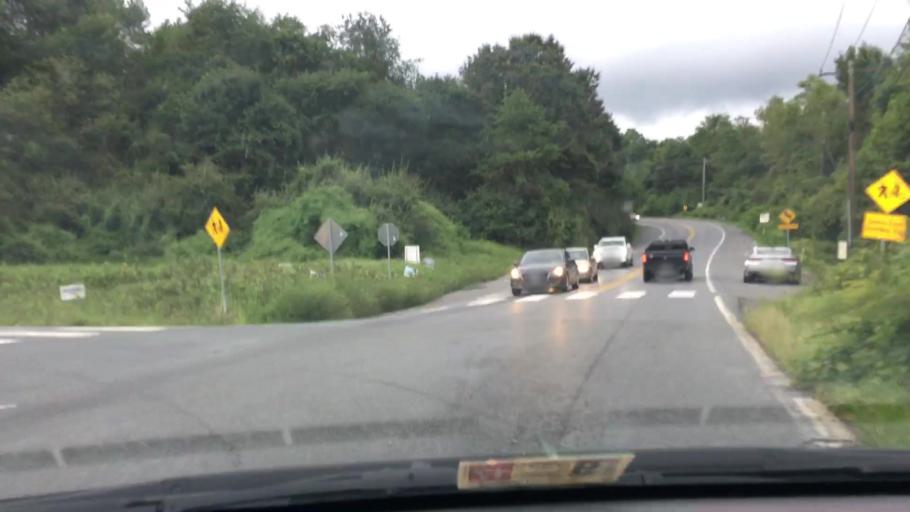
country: US
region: Maryland
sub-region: Montgomery County
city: Montgomery Village
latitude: 39.2012
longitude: -77.2039
